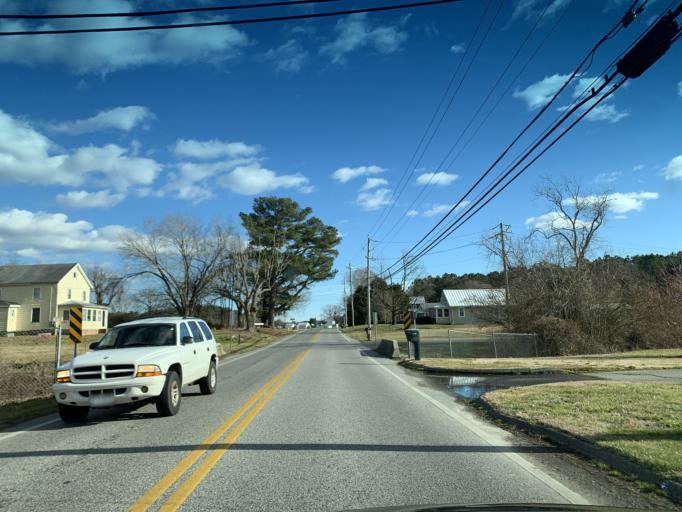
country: US
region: Maryland
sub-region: Worcester County
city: Berlin
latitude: 38.3221
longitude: -75.2050
